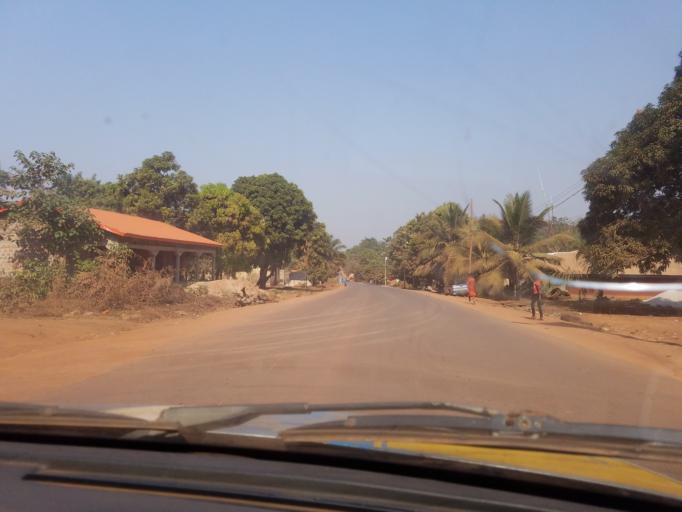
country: GN
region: Boke
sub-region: Boke Prefecture
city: Sangueya
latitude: 10.8002
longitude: -14.3933
